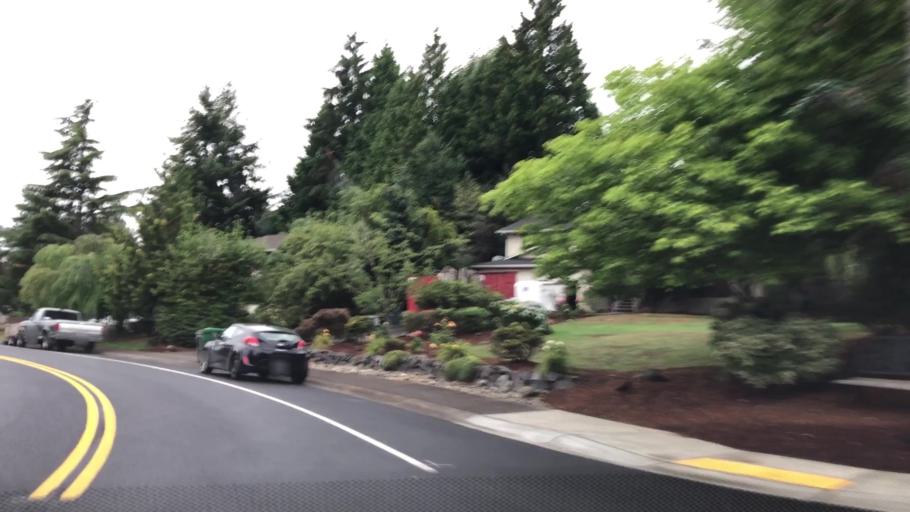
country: US
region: Washington
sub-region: Snohomish County
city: North Creek
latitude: 47.8286
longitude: -122.1996
